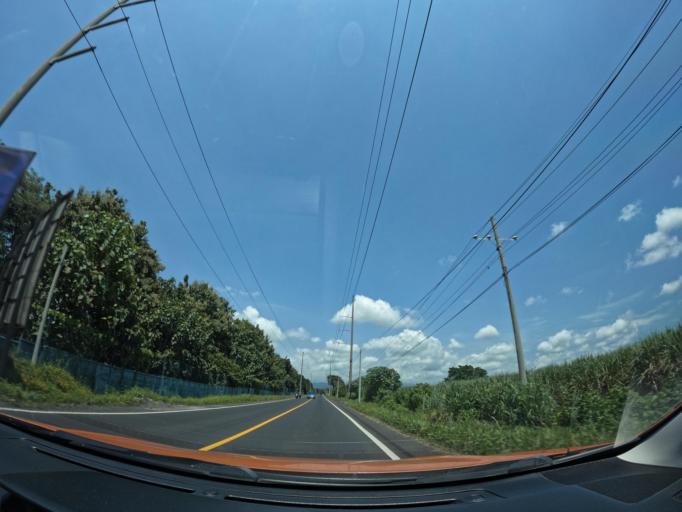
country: GT
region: Escuintla
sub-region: Municipio de Escuintla
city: Escuintla
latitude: 14.2526
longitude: -90.8036
